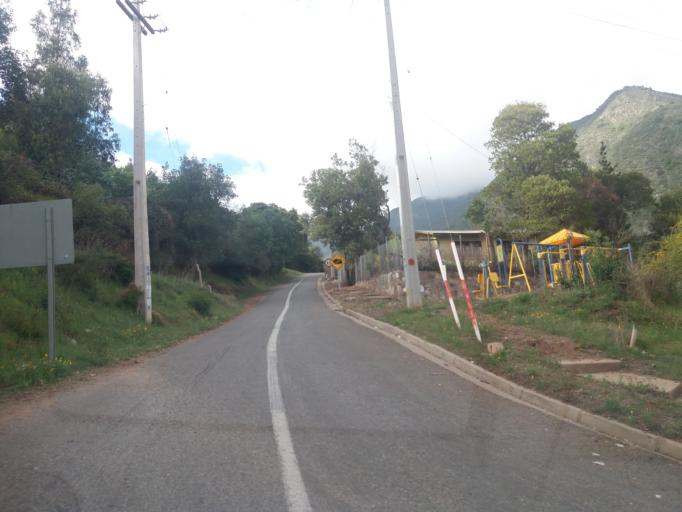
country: CL
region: Valparaiso
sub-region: Provincia de Marga Marga
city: Limache
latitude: -33.0646
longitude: -71.0648
